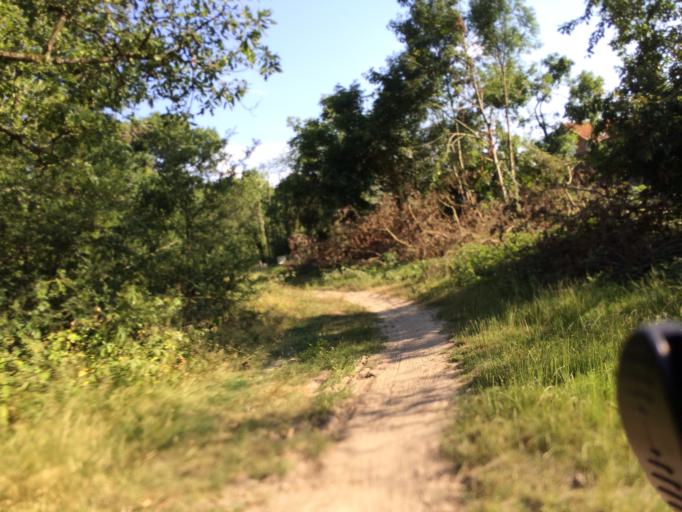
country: FR
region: Ile-de-France
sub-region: Departement de l'Essonne
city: Soisy-sur-Seine
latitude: 48.6540
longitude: 2.4679
